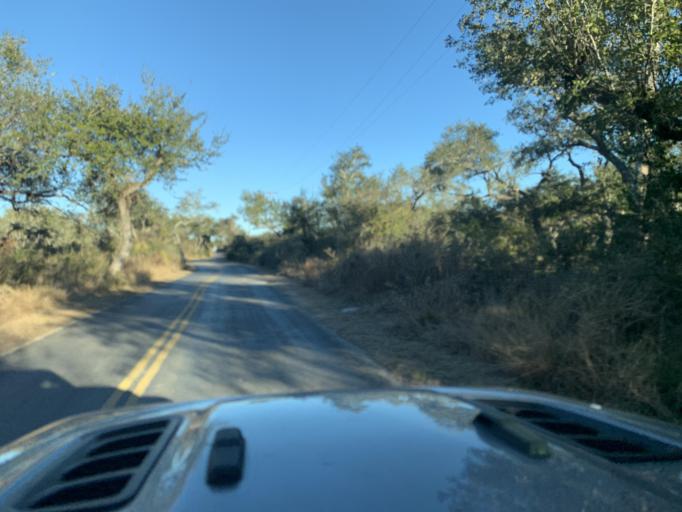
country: US
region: Texas
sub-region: Aransas County
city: Fulton
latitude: 28.1518
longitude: -96.9834
